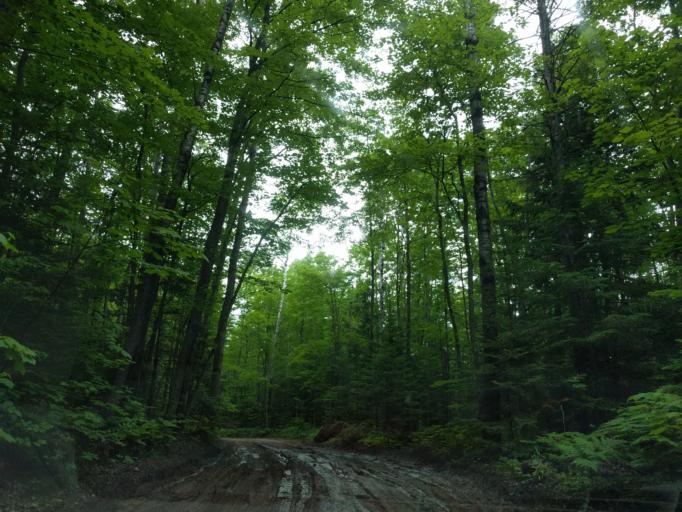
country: US
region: Michigan
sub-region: Marquette County
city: Trowbridge Park
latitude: 46.5993
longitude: -87.4960
